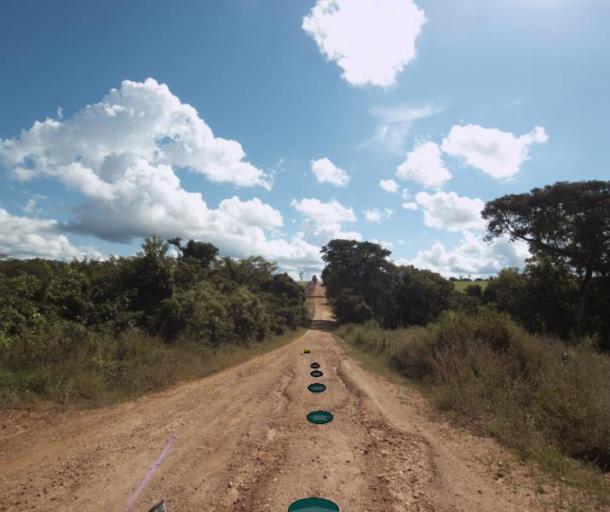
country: BR
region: Goias
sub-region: Pirenopolis
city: Pirenopolis
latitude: -15.8285
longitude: -49.1287
